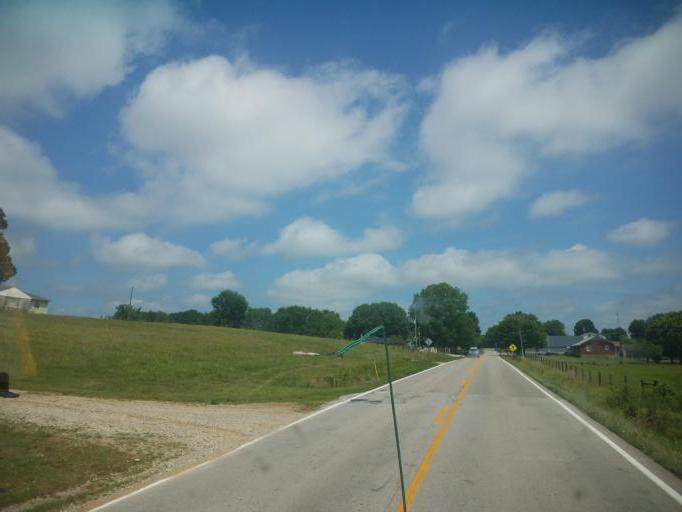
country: US
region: Kentucky
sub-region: Barren County
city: Glasgow
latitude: 36.9153
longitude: -85.7859
